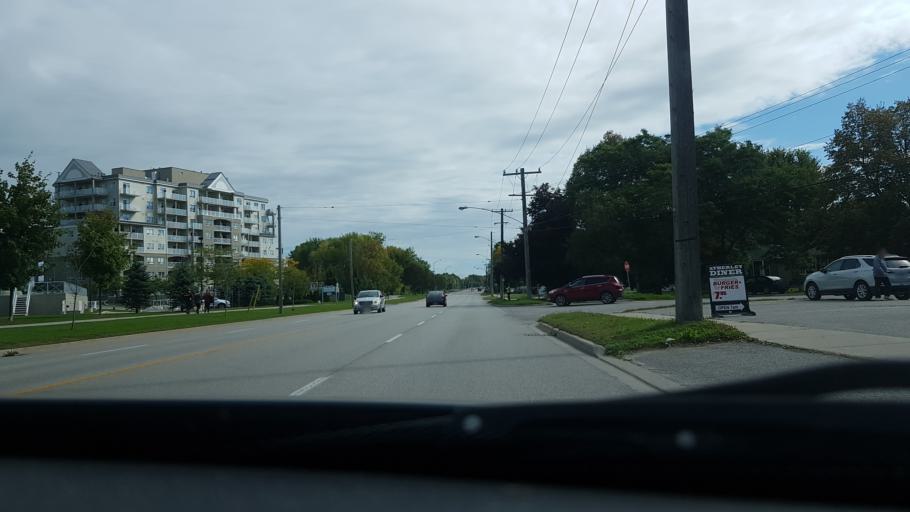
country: CA
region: Ontario
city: Orillia
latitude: 44.6059
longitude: -79.3942
